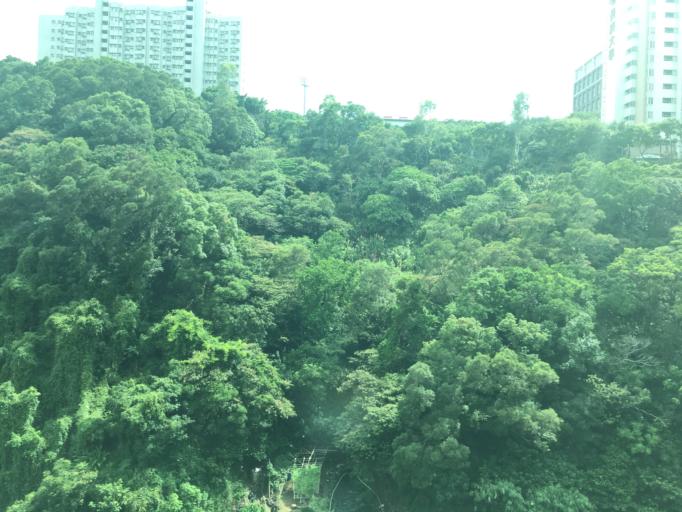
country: TW
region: Taipei
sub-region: Taipei
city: Banqiao
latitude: 25.0347
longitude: 121.3931
